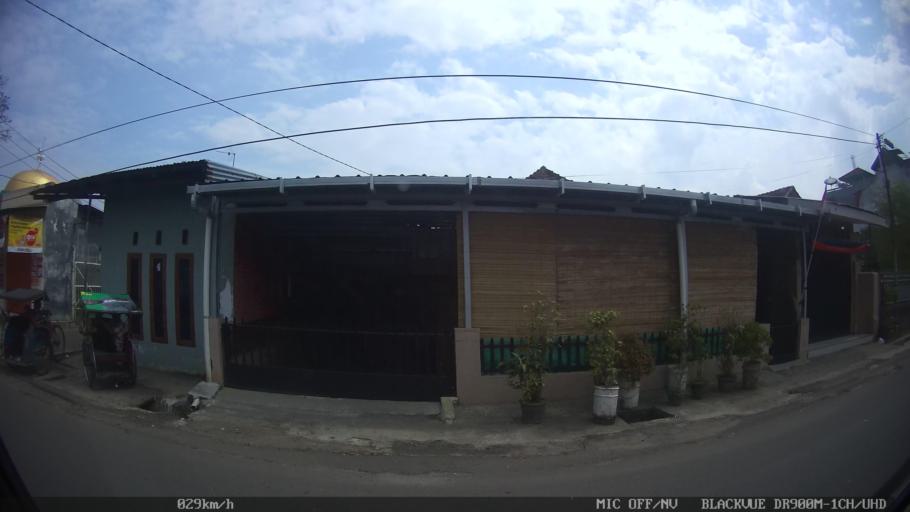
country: ID
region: Lampung
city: Bandarlampung
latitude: -5.4121
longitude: 105.2527
